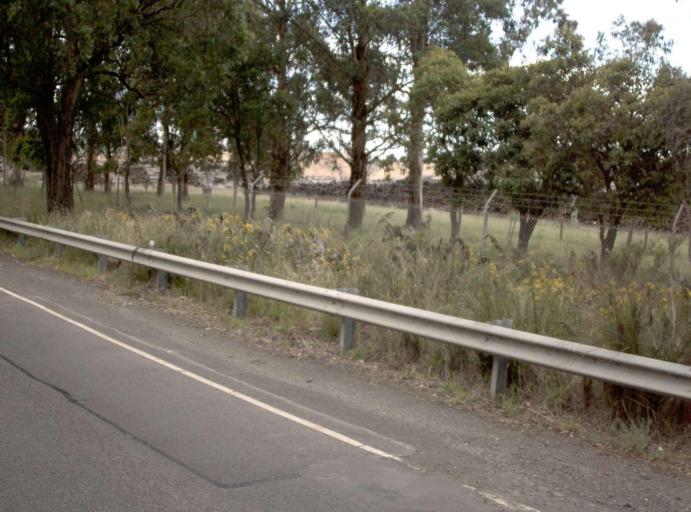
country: AU
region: Victoria
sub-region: Latrobe
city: Morwell
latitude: -38.1902
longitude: 146.4390
